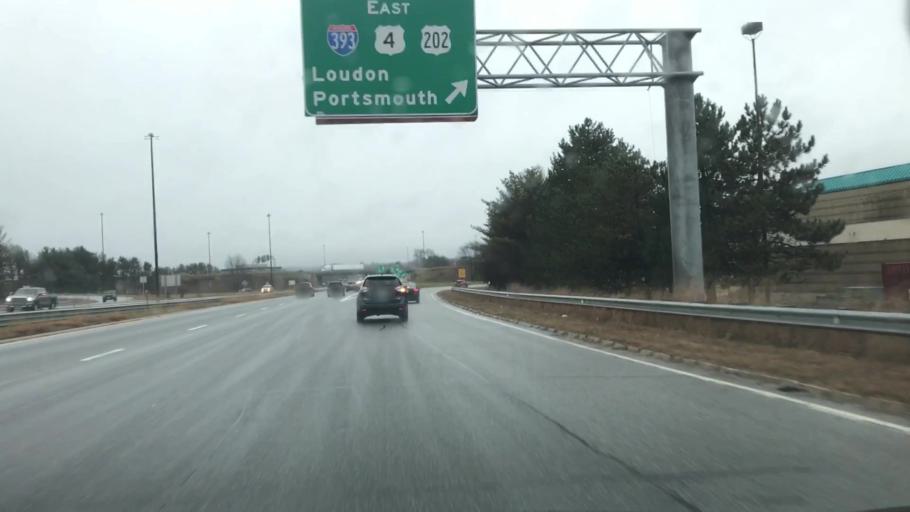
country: US
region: New Hampshire
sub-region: Merrimack County
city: Concord
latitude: 43.2126
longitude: -71.5337
